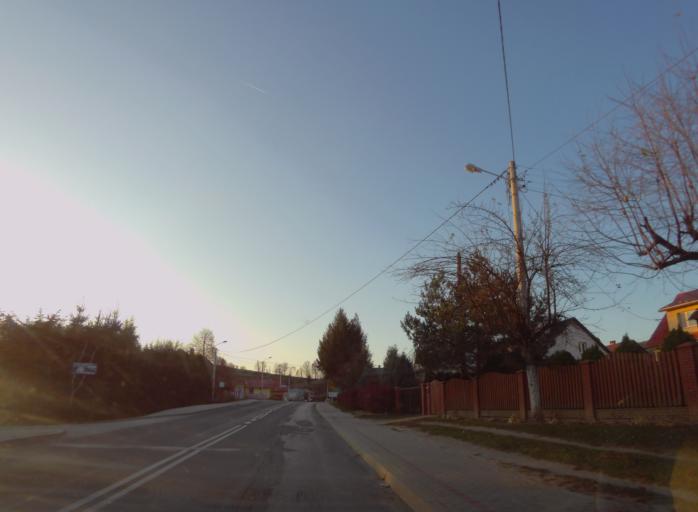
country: PL
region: Subcarpathian Voivodeship
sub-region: Powiat leski
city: Lesko
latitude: 49.4235
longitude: 22.3271
